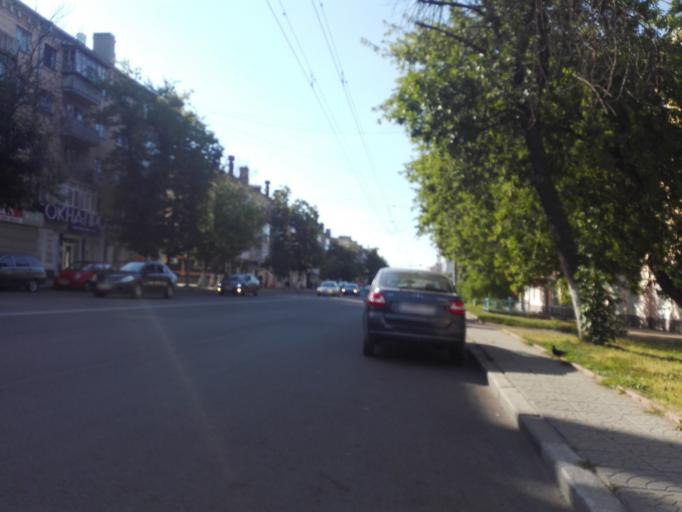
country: RU
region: Orjol
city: Orel
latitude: 52.9720
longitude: 36.0847
